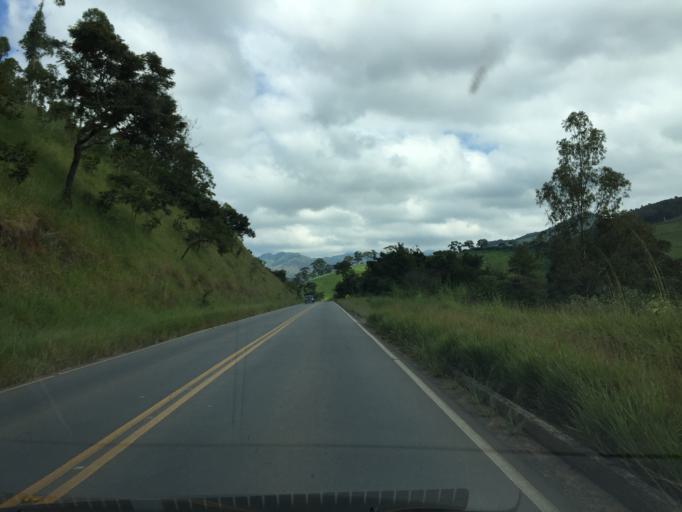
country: BR
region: Minas Gerais
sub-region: Passa Quatro
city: Passa Quatro
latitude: -22.3689
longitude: -44.9604
